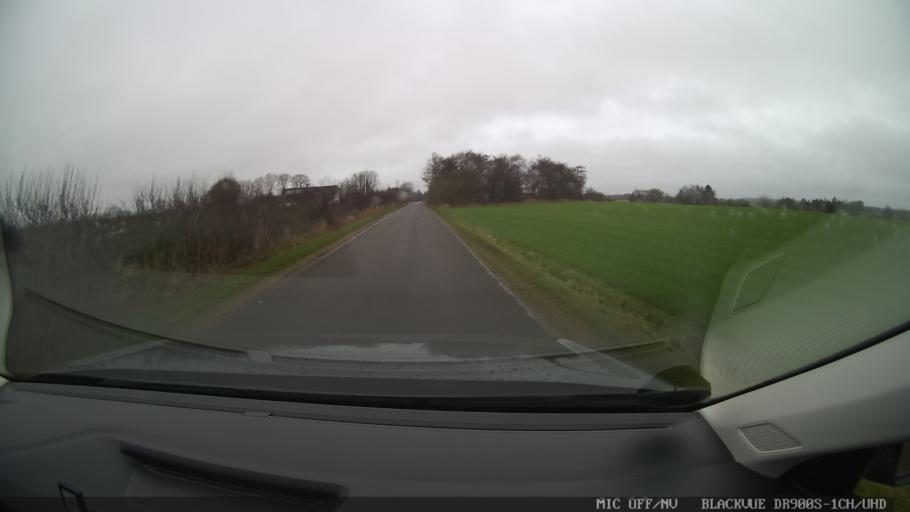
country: DK
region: Central Jutland
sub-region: Viborg Kommune
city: Karup
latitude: 56.3139
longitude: 9.2475
